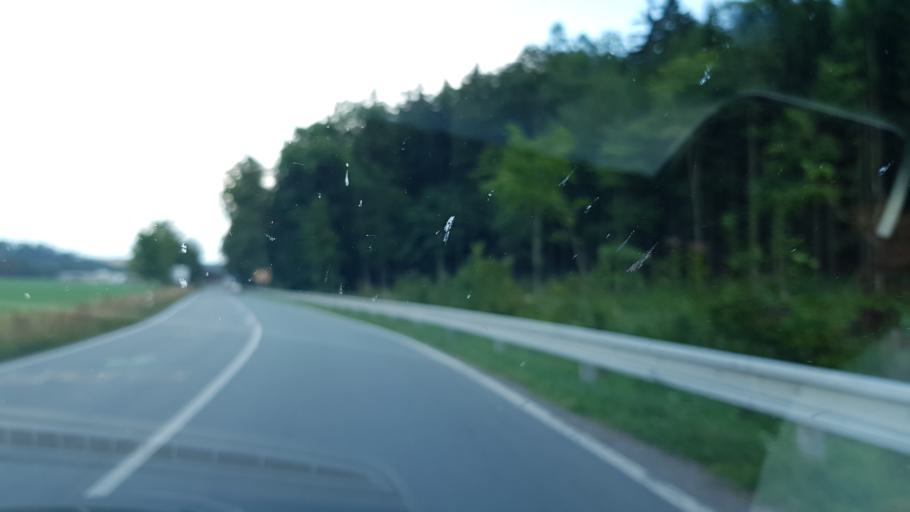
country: CZ
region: Pardubicky
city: Zamberk
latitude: 50.0838
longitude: 16.4775
